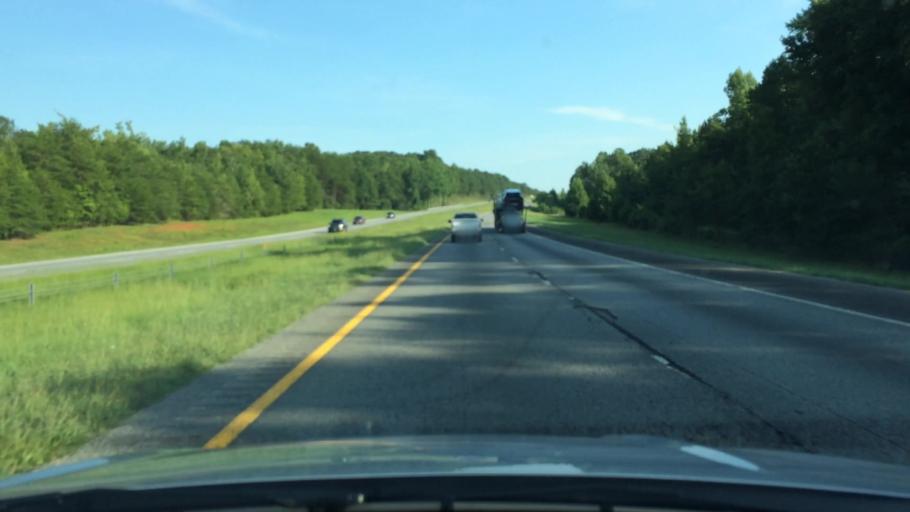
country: US
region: South Carolina
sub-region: Spartanburg County
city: Roebuck
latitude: 34.8226
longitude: -81.9644
